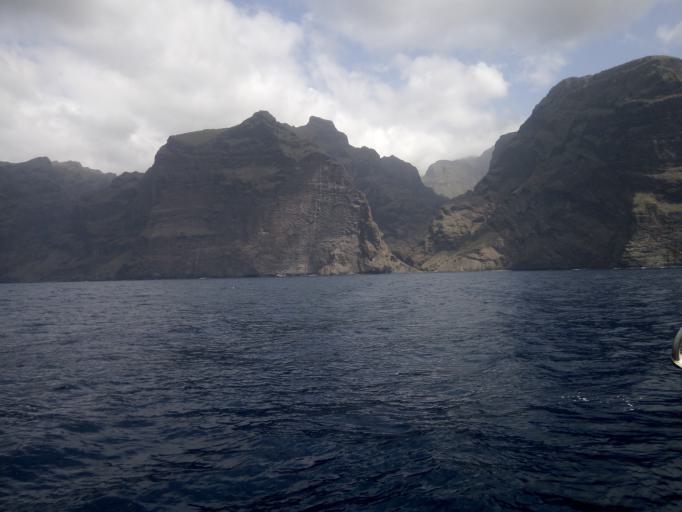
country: ES
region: Canary Islands
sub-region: Provincia de Santa Cruz de Tenerife
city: Santiago del Teide
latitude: 28.2789
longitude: -16.8758
